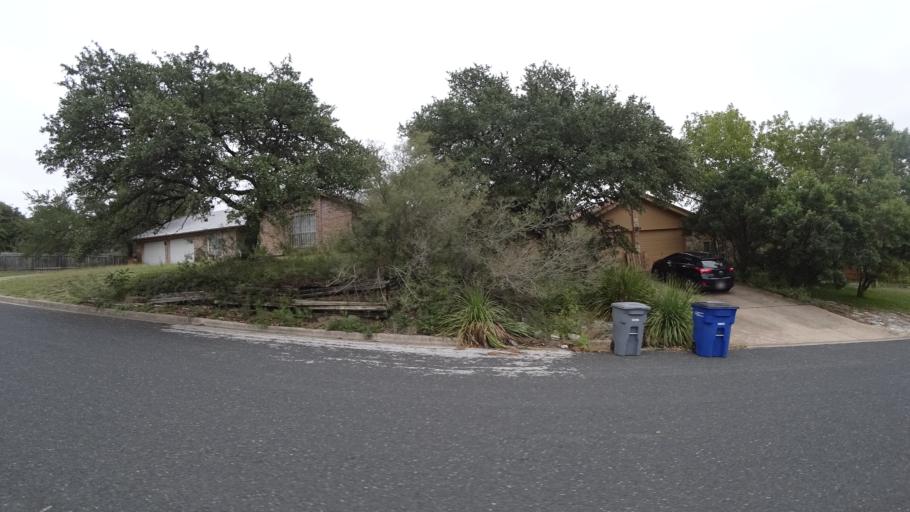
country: US
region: Texas
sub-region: Travis County
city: Barton Creek
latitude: 30.2397
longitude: -97.8919
